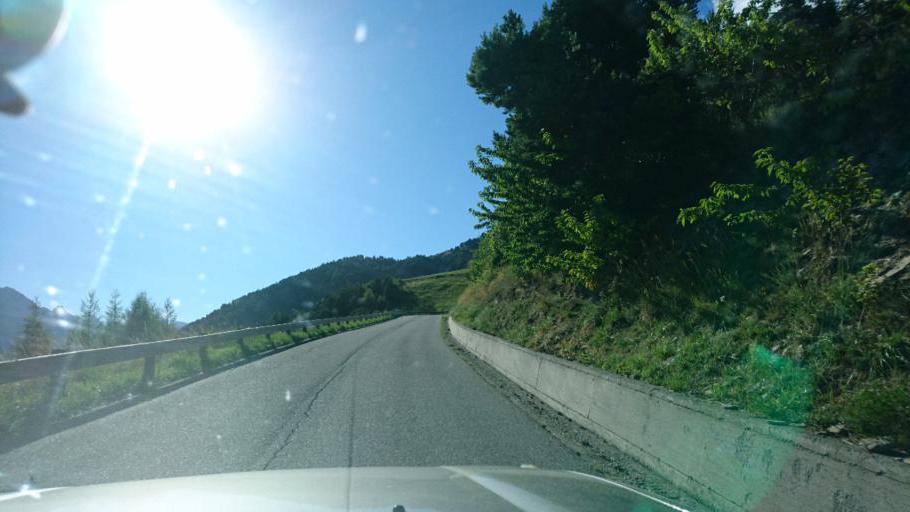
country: IT
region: Aosta Valley
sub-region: Valle d'Aosta
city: Saint-Nicolas
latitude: 45.7263
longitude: 7.1874
